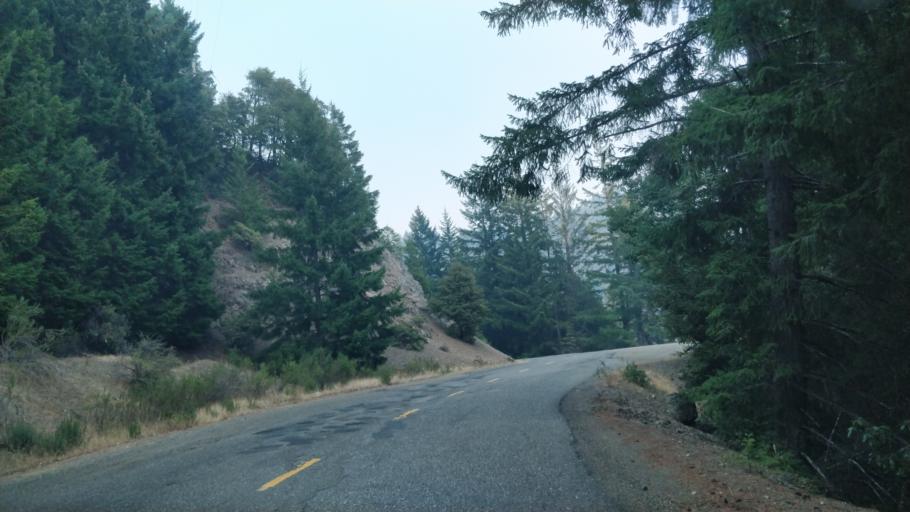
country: US
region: California
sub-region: Humboldt County
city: Rio Dell
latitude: 40.2733
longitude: -124.0790
